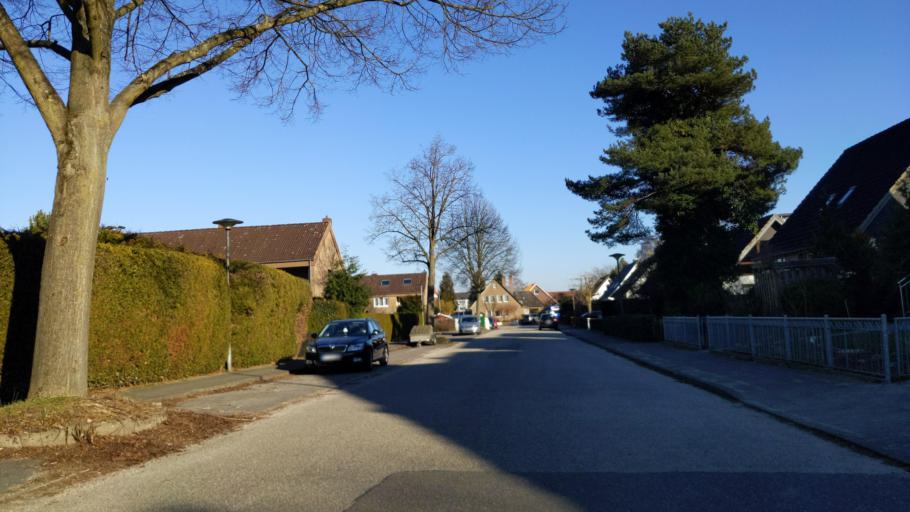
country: DE
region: Schleswig-Holstein
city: Luebeck
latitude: 53.8756
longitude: 10.7156
